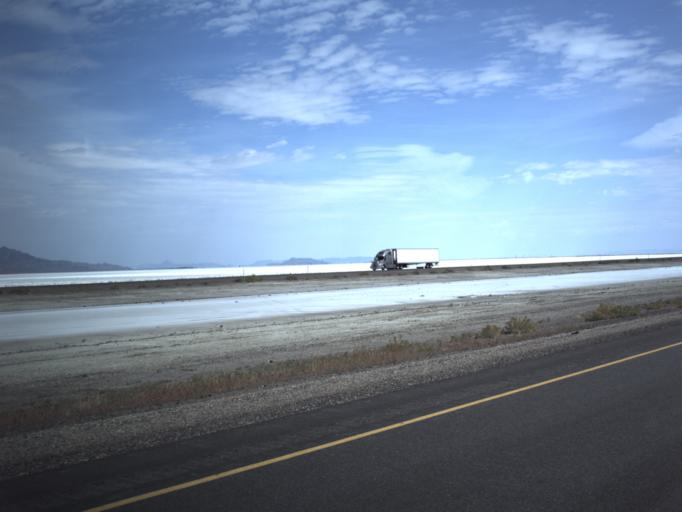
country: US
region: Utah
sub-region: Tooele County
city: Wendover
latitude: 40.7399
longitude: -113.9252
